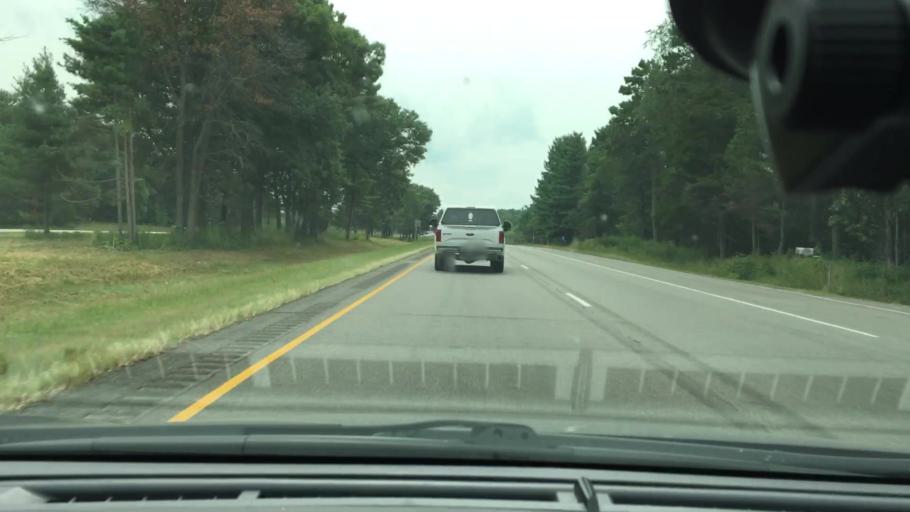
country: US
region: Minnesota
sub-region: Mille Lacs County
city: Princeton
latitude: 45.5172
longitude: -93.5832
